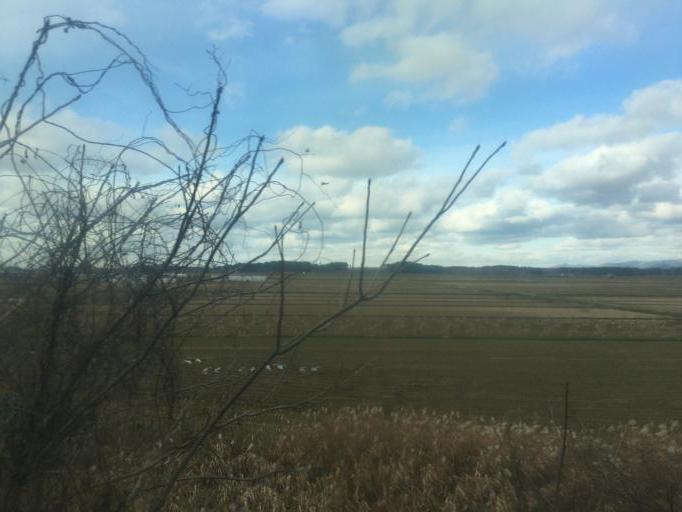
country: JP
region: Akita
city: Noshiromachi
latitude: 40.2003
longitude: 140.1044
